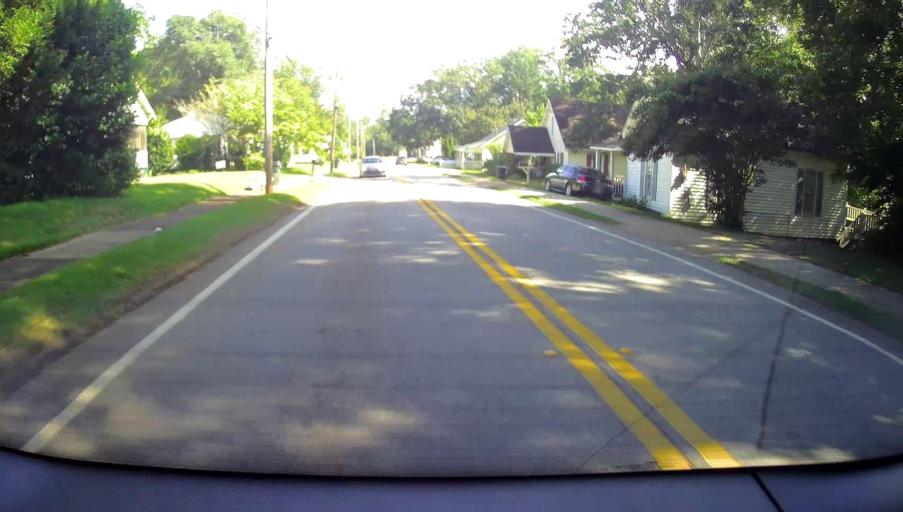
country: US
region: Georgia
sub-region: Upson County
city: Thomaston
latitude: 32.8919
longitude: -84.3346
